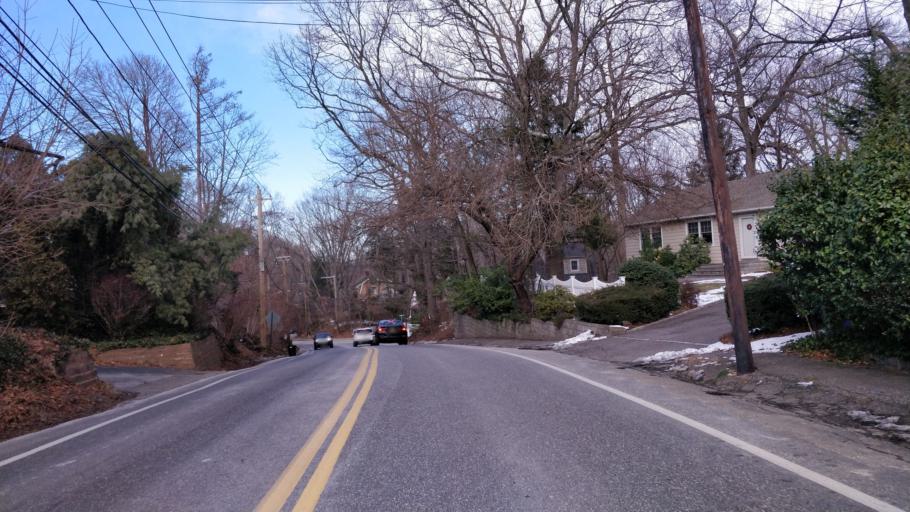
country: US
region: New York
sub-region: Suffolk County
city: Northport
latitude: 40.8960
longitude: -73.3426
